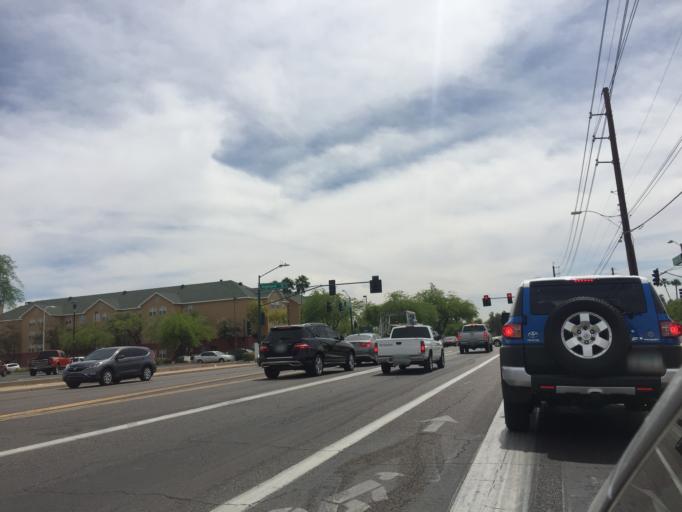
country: US
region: Arizona
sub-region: Maricopa County
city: Phoenix
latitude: 33.5063
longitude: -112.0389
